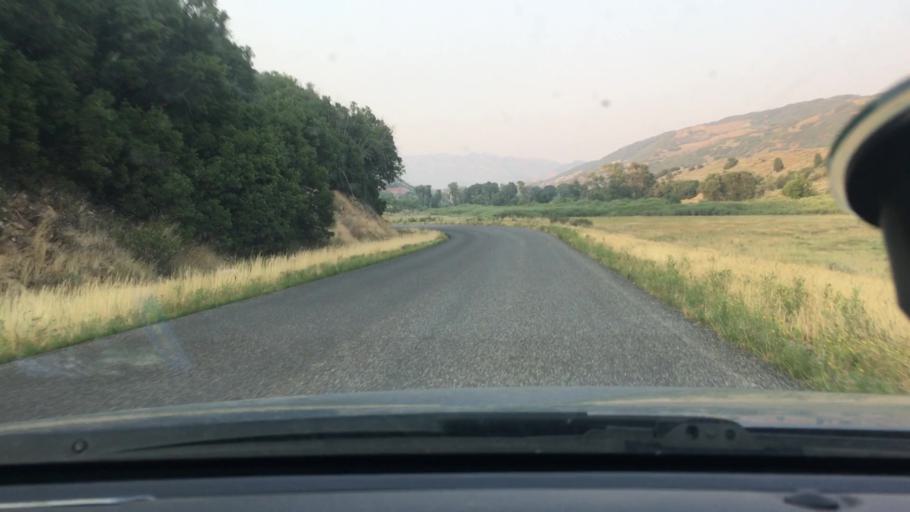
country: US
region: Utah
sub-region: Utah County
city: Mapleton
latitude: 40.0320
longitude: -111.4990
